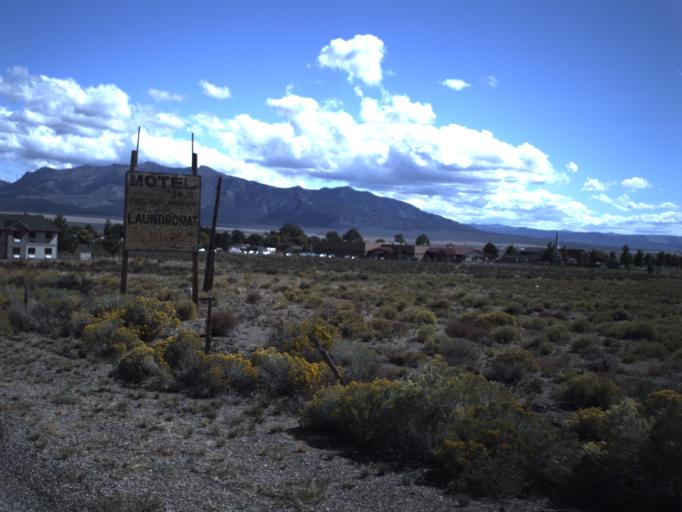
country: US
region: Utah
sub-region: Beaver County
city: Milford
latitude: 38.3971
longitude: -113.0230
